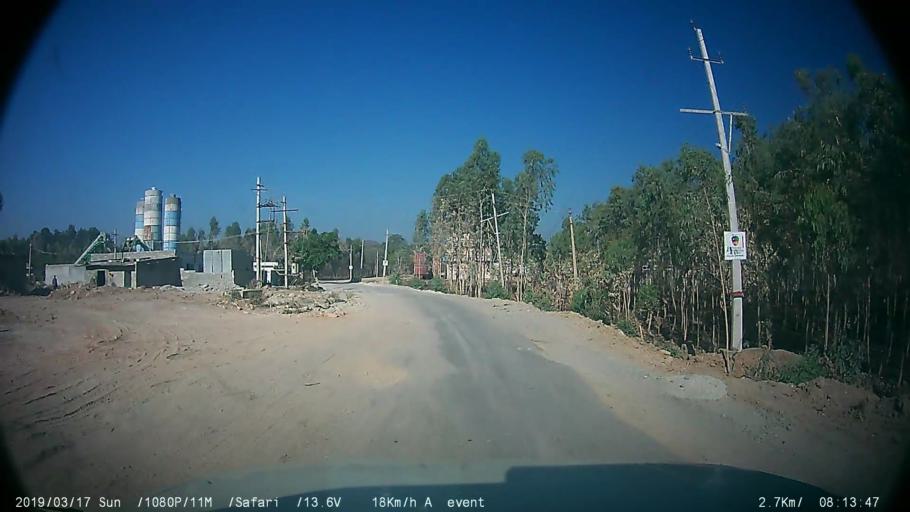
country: IN
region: Karnataka
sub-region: Bangalore Urban
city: Anekal
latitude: 12.8141
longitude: 77.6316
